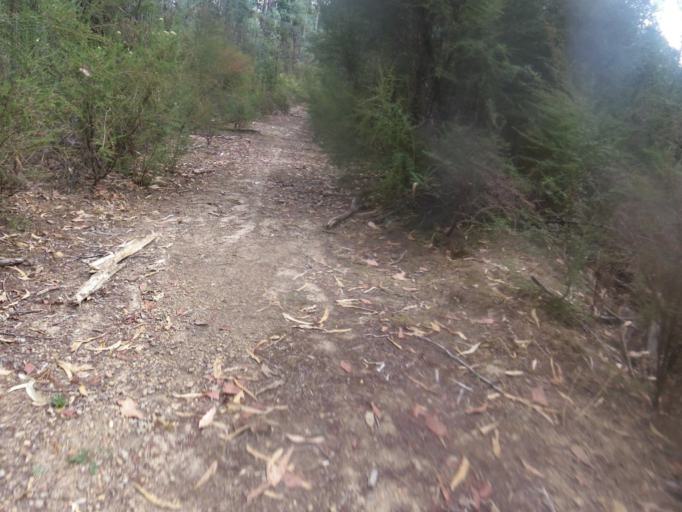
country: AU
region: Victoria
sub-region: Murrindindi
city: Alexandra
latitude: -37.3794
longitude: 145.5583
